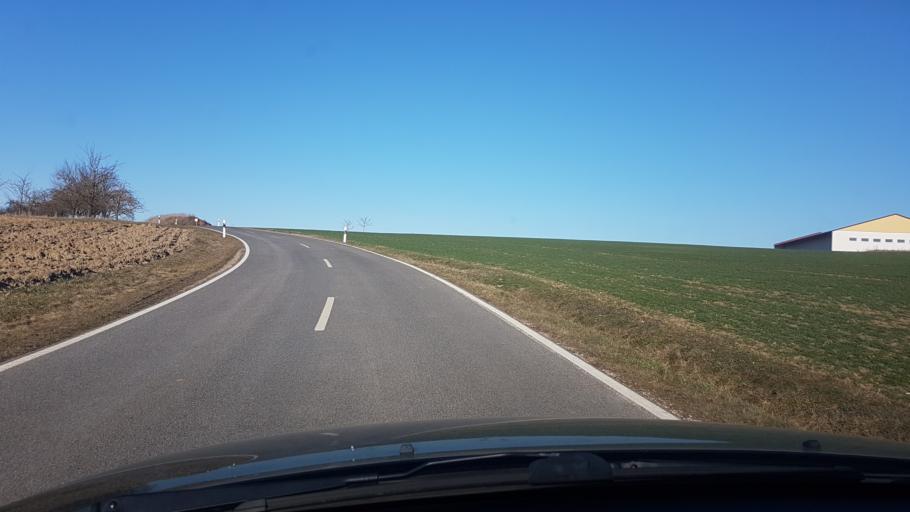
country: DE
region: Bavaria
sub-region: Upper Franconia
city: Zapfendorf
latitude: 50.0092
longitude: 10.9771
